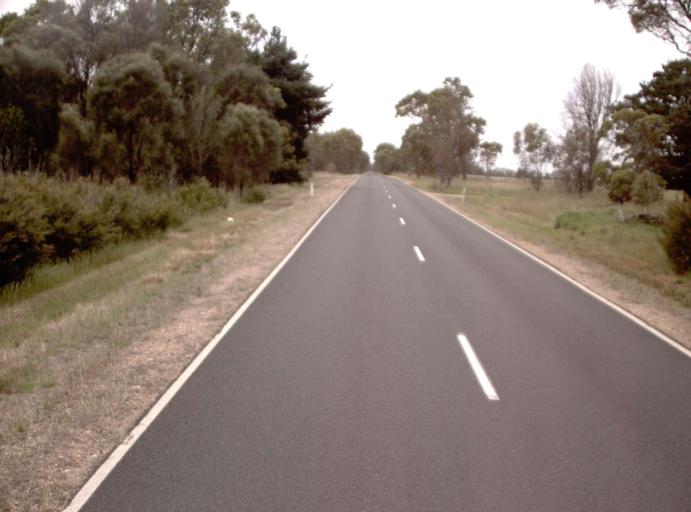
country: AU
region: Victoria
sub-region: Wellington
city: Sale
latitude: -37.9702
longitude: 147.1432
